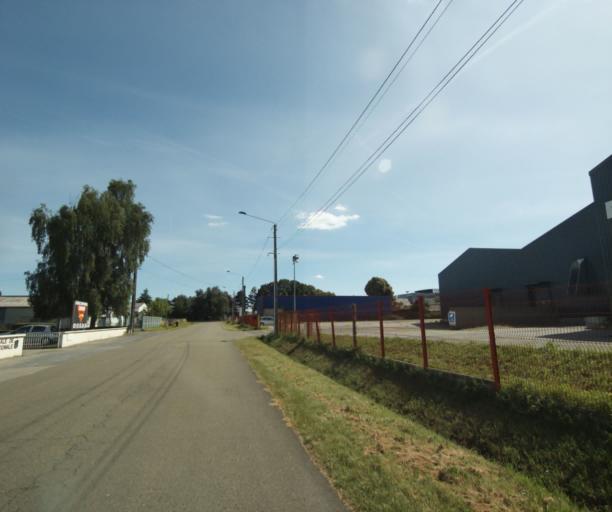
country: FR
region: Pays de la Loire
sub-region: Departement de la Mayenne
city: Change
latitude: 48.0722
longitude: -0.7981
